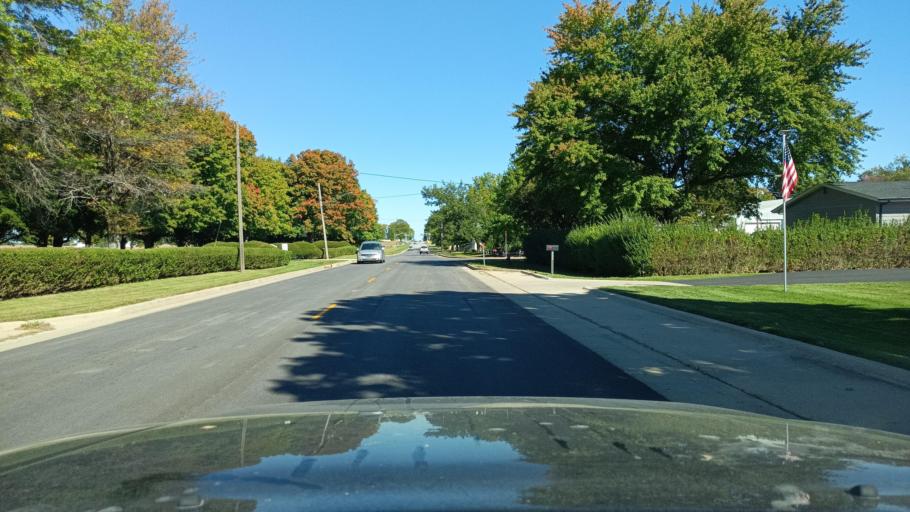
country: US
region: Illinois
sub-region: Champaign County
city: Philo
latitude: 40.0030
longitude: -88.1613
